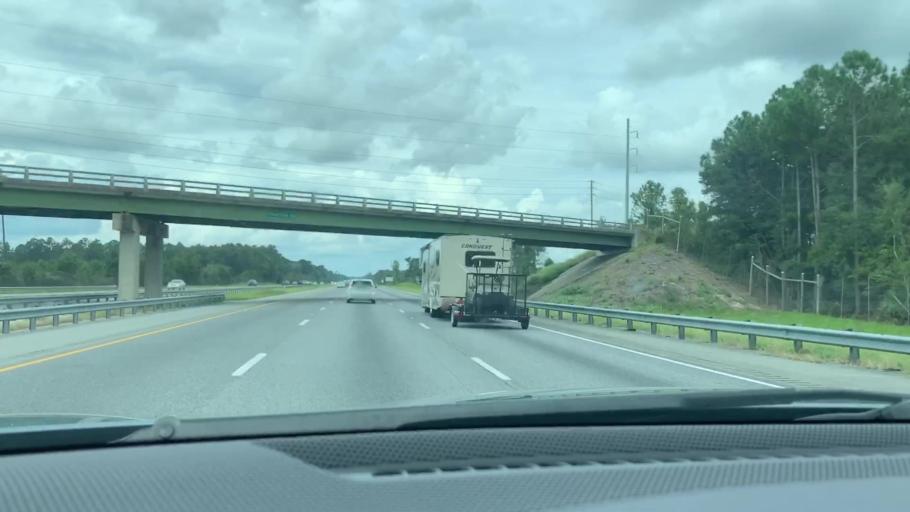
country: US
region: Georgia
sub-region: McIntosh County
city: Darien
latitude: 31.4314
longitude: -81.4434
